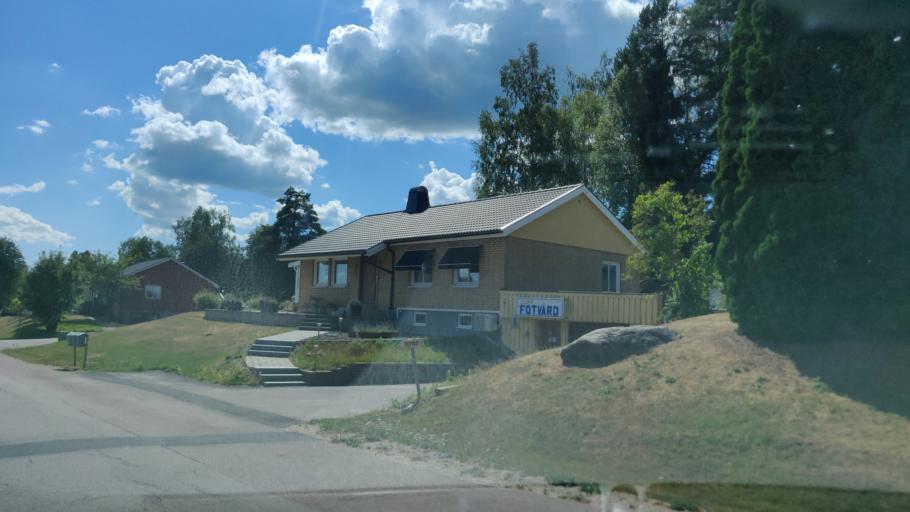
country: SE
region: Vaermland
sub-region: Hagfors Kommun
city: Ekshaerad
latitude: 60.1806
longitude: 13.4949
